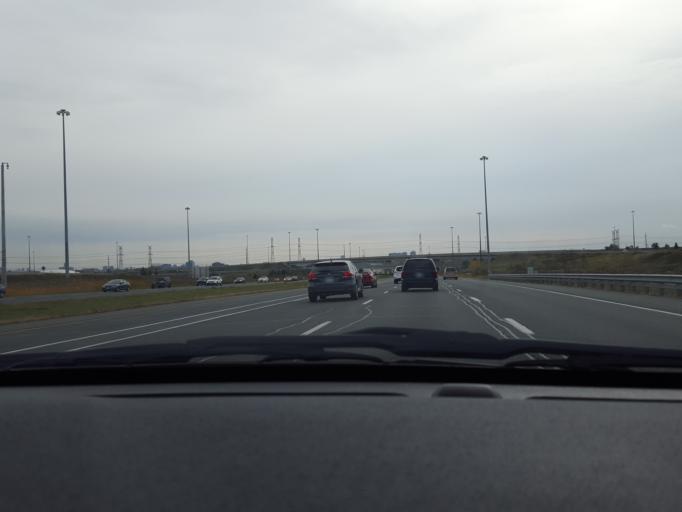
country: CA
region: Ontario
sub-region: York
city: Richmond Hill
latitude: 43.8449
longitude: -79.3707
